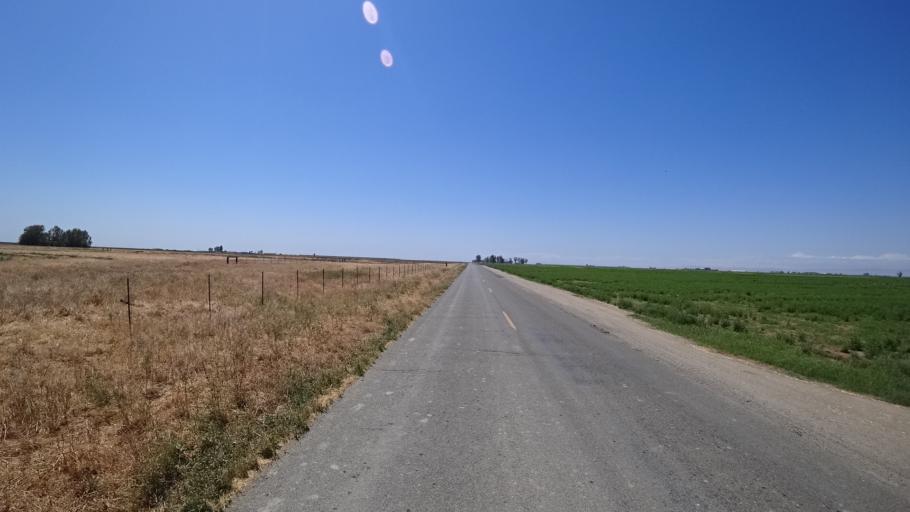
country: US
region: California
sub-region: Kings County
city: Stratford
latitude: 36.1987
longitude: -119.7624
